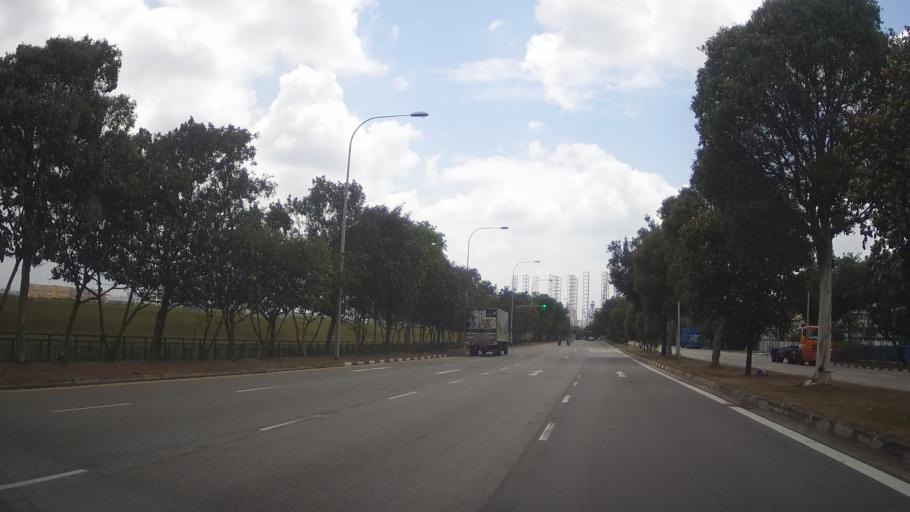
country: SG
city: Singapore
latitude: 1.3080
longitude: 103.7397
